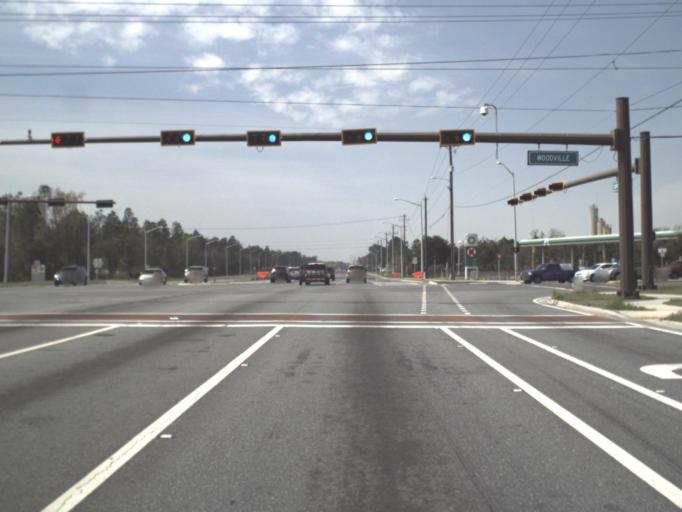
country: US
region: Florida
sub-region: Leon County
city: Tallahassee
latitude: 30.3759
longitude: -84.2696
